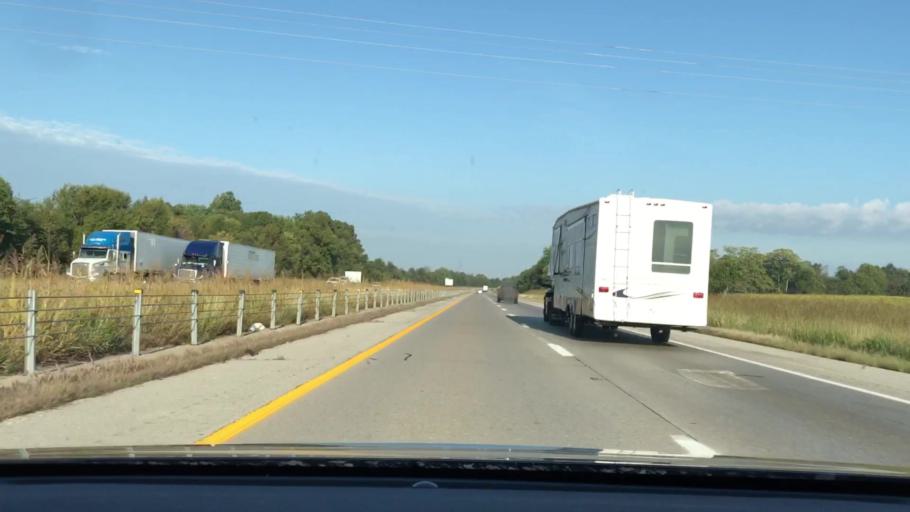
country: US
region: Kentucky
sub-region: Christian County
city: Oak Grove
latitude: 36.7083
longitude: -87.4691
